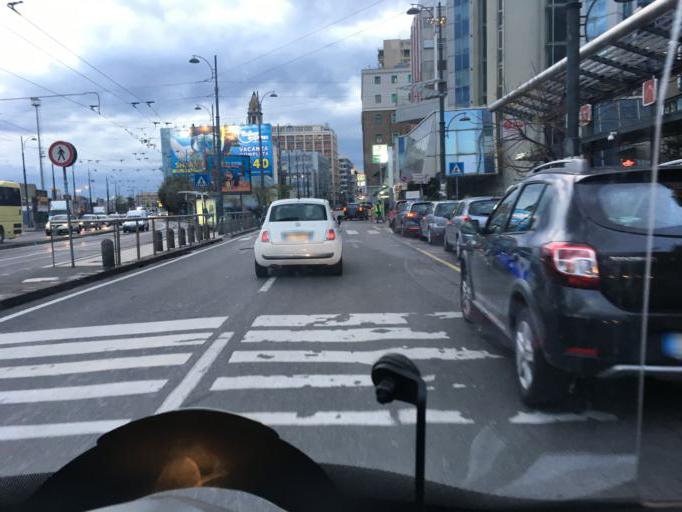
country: IT
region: Campania
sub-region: Provincia di Napoli
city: Napoli
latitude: 40.8439
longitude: 14.2586
